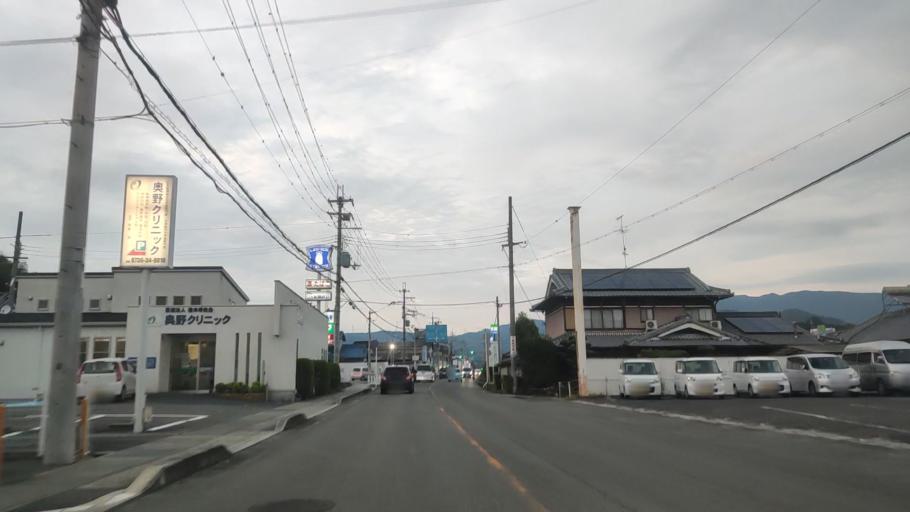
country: JP
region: Wakayama
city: Hashimoto
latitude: 34.3365
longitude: 135.6057
